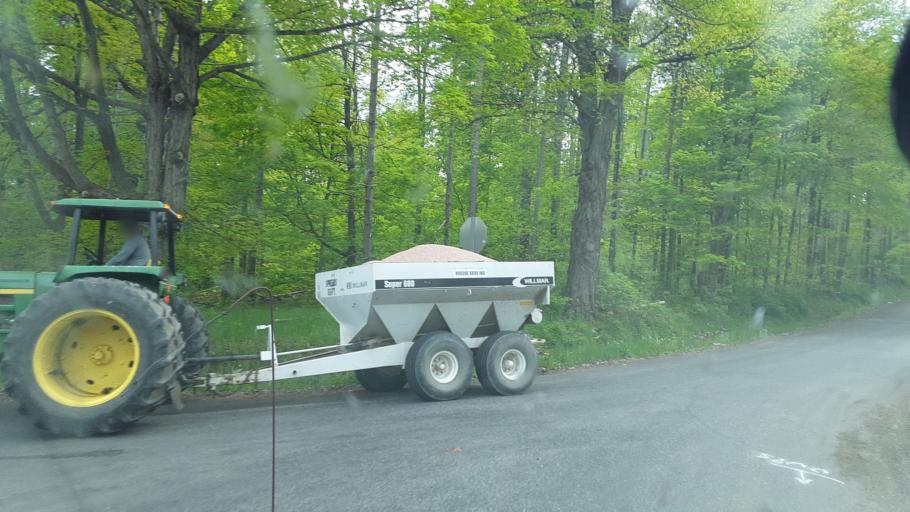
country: US
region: Ohio
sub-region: Portage County
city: Garrettsville
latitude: 41.3428
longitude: -81.0415
